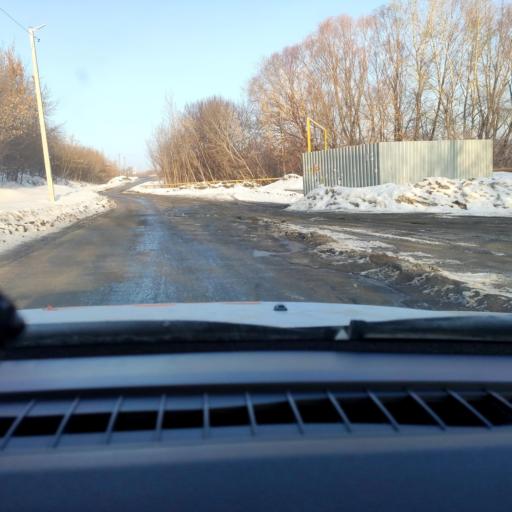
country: RU
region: Samara
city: Novokuybyshevsk
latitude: 53.1201
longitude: 49.9452
